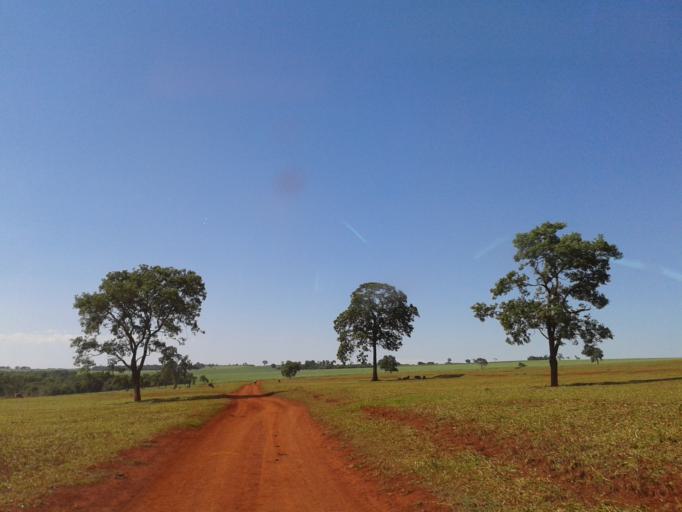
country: BR
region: Minas Gerais
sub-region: Centralina
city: Centralina
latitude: -18.6249
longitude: -49.2585
